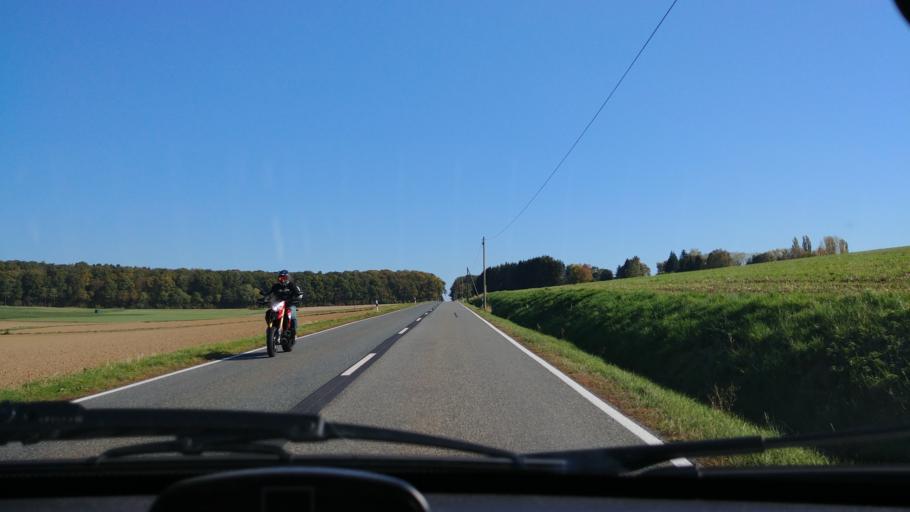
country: DE
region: Rheinland-Pfalz
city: Allendorf
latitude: 50.2728
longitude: 7.9976
